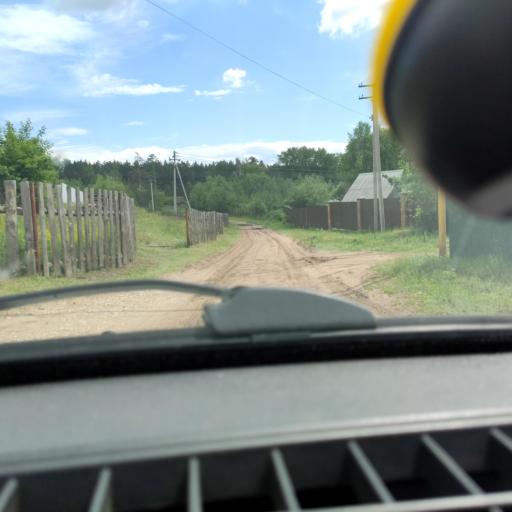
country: RU
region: Samara
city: Povolzhskiy
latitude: 53.6374
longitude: 49.6837
